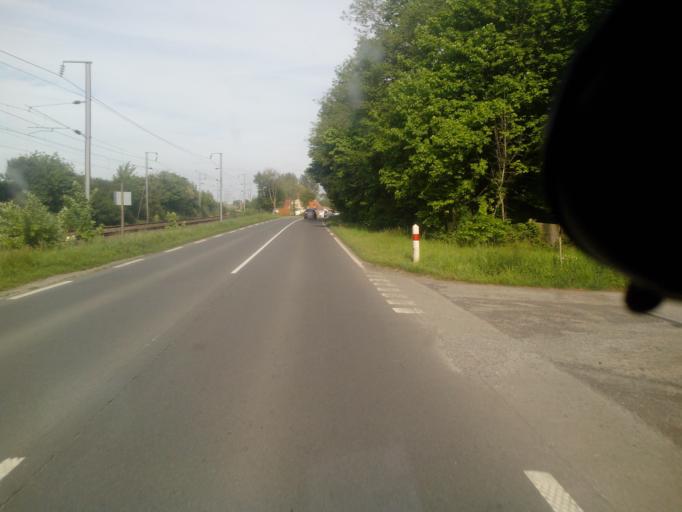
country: FR
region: Nord-Pas-de-Calais
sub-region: Departement du Nord
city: Blaringhem
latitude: 50.7303
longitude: 2.4254
